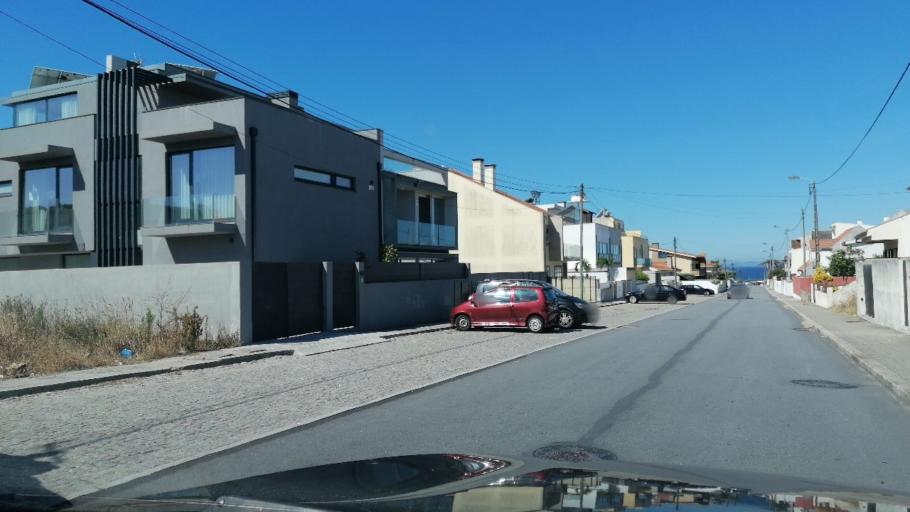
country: PT
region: Porto
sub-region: Matosinhos
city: Lavra
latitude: 41.2515
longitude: -8.7198
